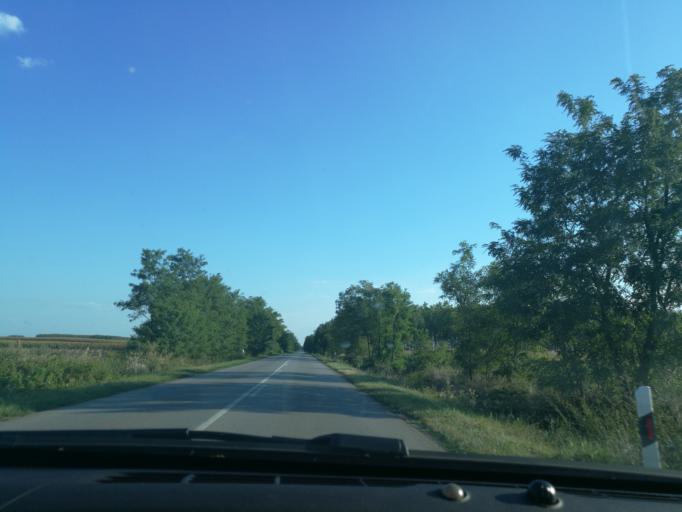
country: HU
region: Szabolcs-Szatmar-Bereg
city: Tiszabercel
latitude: 48.1369
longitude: 21.6471
